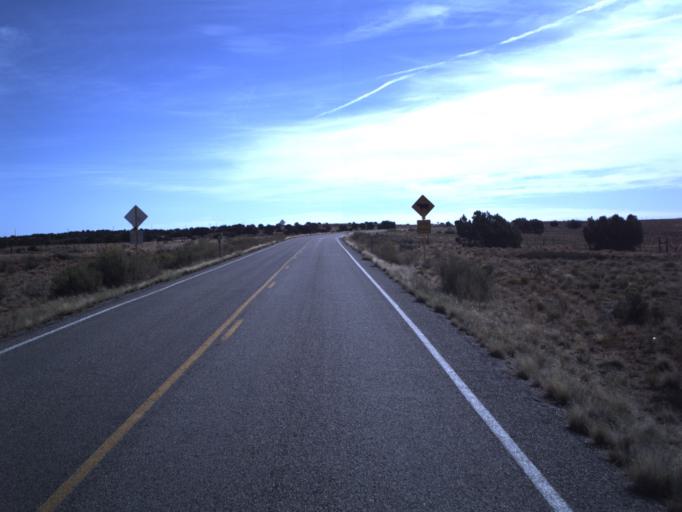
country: US
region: Utah
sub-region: San Juan County
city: Blanding
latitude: 37.4359
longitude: -109.3873
